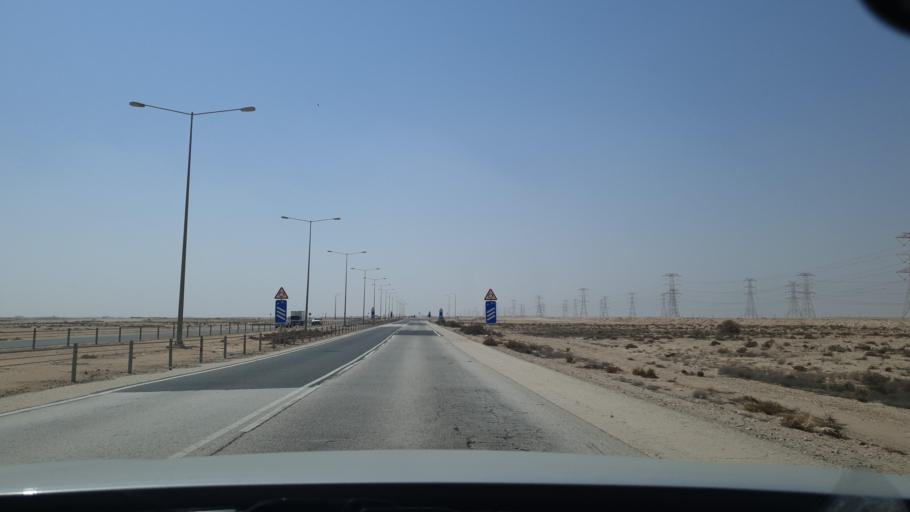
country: QA
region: Al Khawr
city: Al Khawr
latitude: 25.7351
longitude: 51.4584
